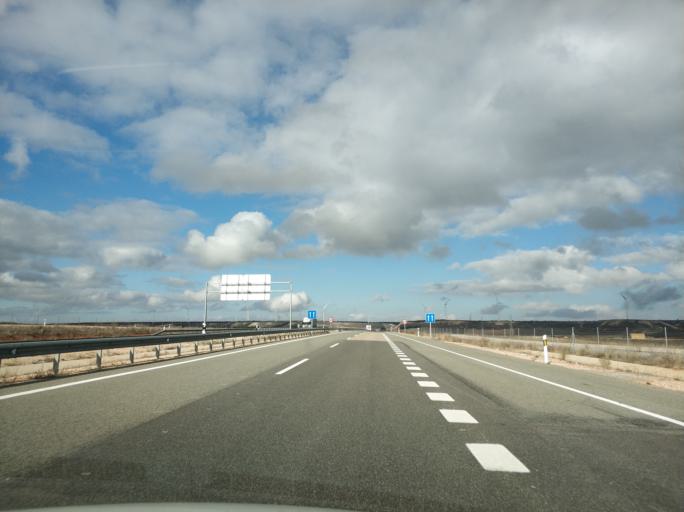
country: ES
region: Castille and Leon
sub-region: Provincia de Soria
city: Alcubilla de las Penas
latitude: 41.2661
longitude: -2.4739
